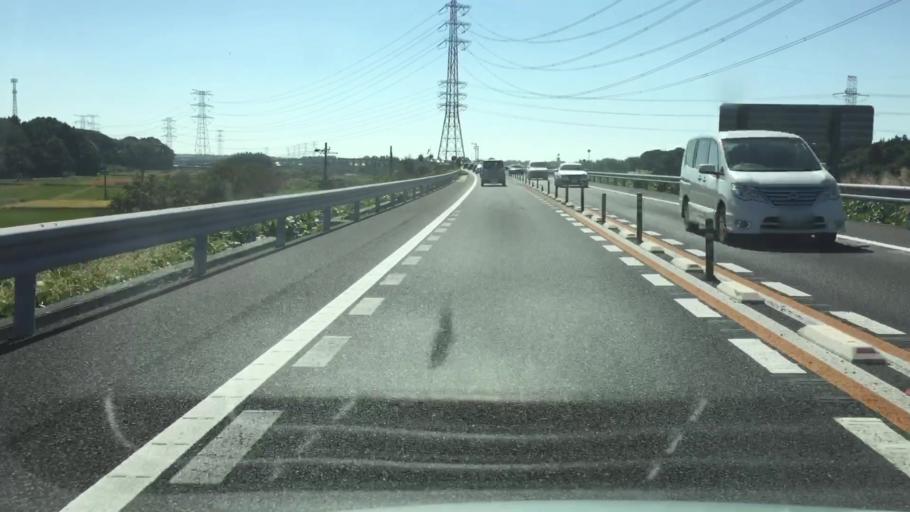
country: JP
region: Ibaraki
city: Ushiku
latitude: 36.0053
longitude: 140.1453
